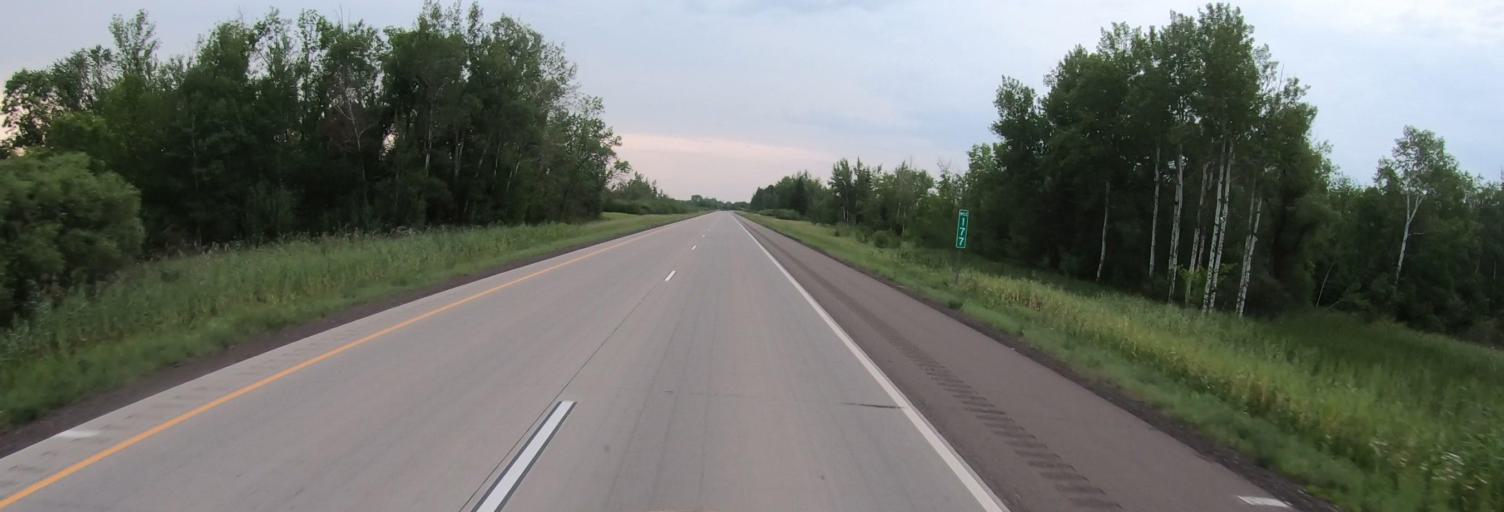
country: US
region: Minnesota
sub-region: Pine County
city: Hinckley
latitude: 45.9291
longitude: -92.9665
